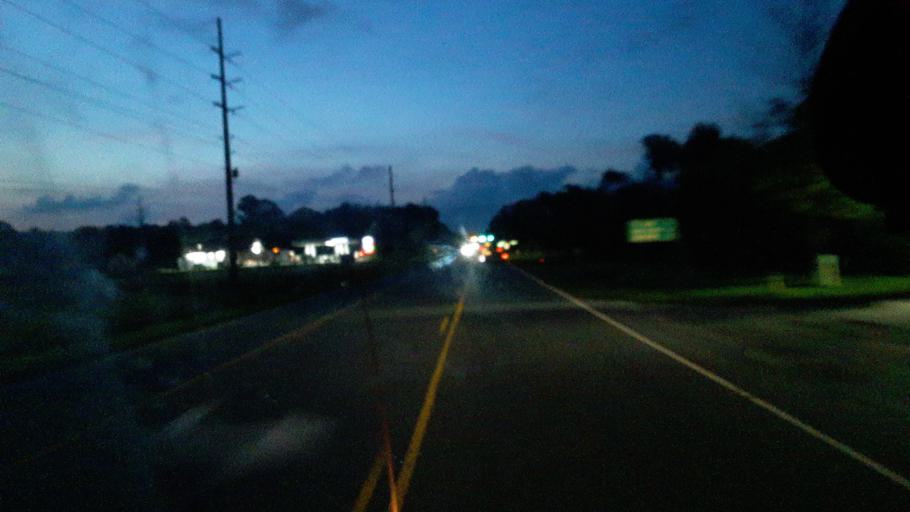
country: US
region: North Carolina
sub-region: Brunswick County
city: Shallotte
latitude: 34.0164
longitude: -78.2717
